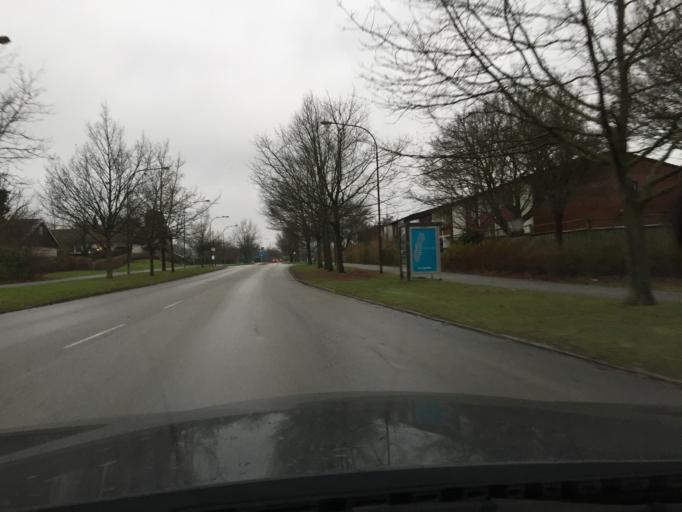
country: SE
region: Skane
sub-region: Lunds Kommun
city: Lund
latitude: 55.7076
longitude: 13.2304
